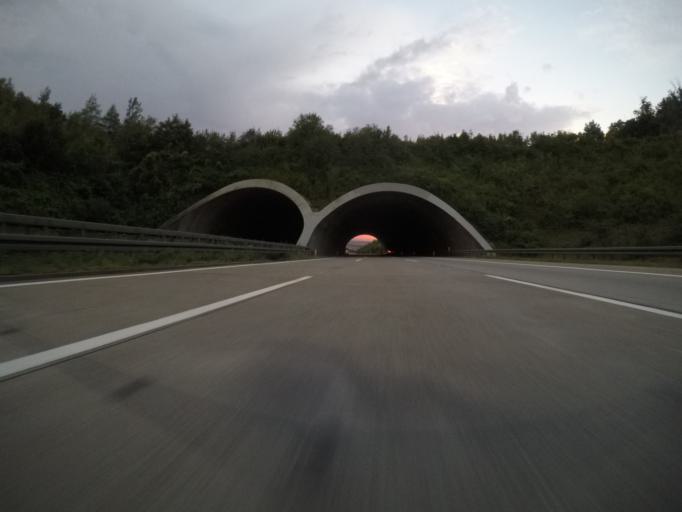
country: DE
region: Baden-Wuerttemberg
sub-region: Regierungsbezirk Stuttgart
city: Aichelberg
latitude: 48.6279
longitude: 9.5766
